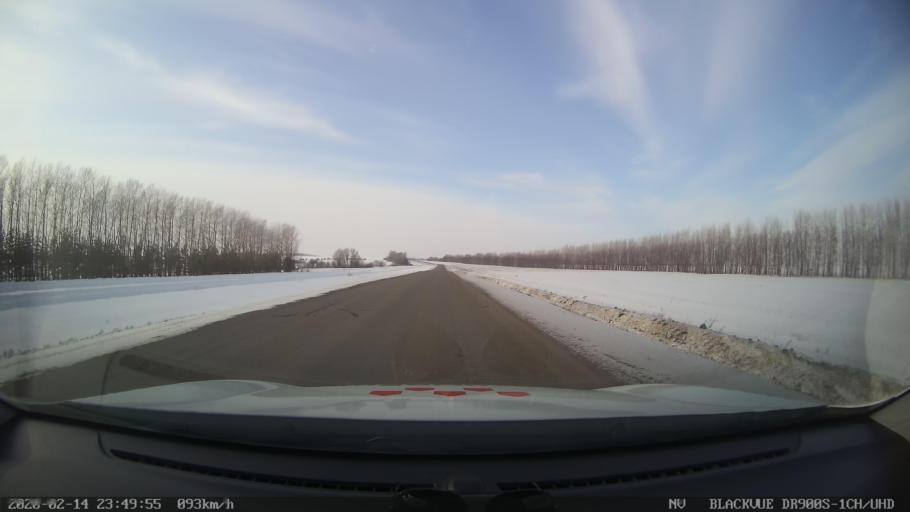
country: RU
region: Tatarstan
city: Kuybyshevskiy Zaton
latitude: 55.2569
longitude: 49.1715
